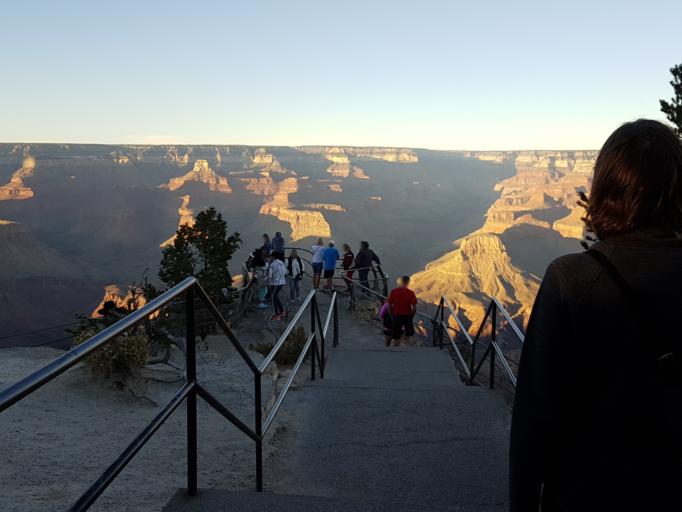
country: US
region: Arizona
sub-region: Coconino County
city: Grand Canyon
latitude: 36.0620
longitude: -112.1089
